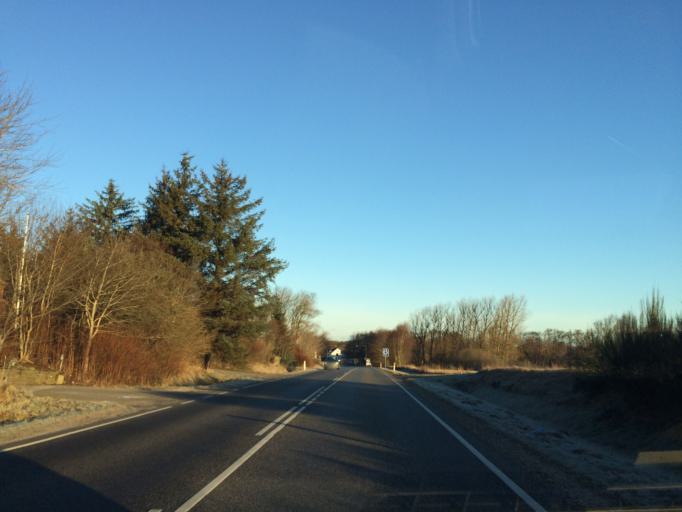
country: DK
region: Central Jutland
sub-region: Holstebro Kommune
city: Ulfborg
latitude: 56.4051
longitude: 8.3146
